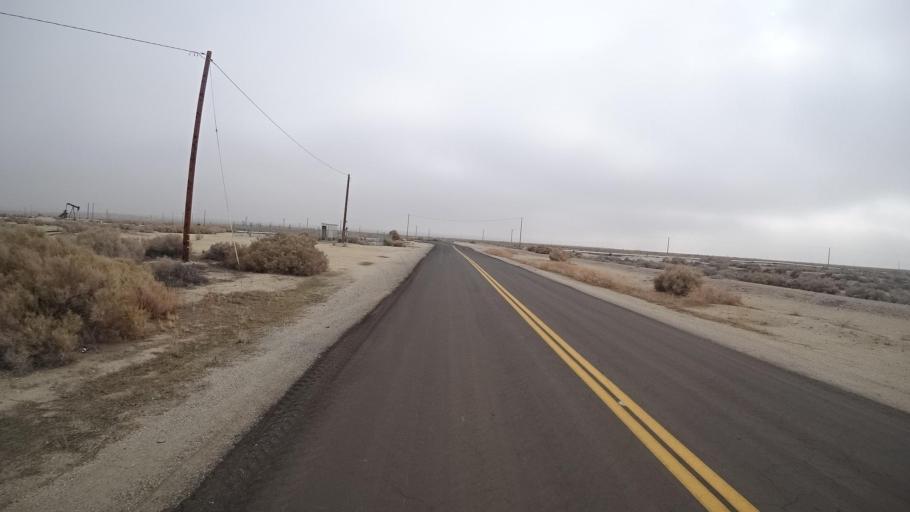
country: US
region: California
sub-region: Kern County
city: Maricopa
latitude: 35.0779
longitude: -119.3786
